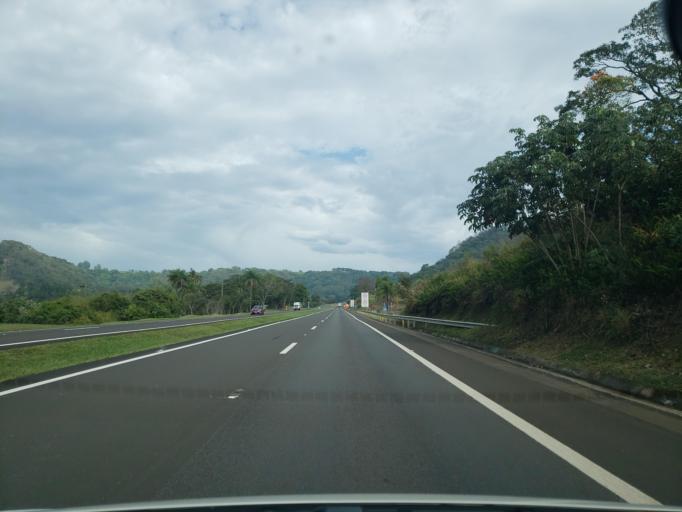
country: BR
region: Sao Paulo
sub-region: Dois Corregos
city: Dois Corregos
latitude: -22.2465
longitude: -48.3300
